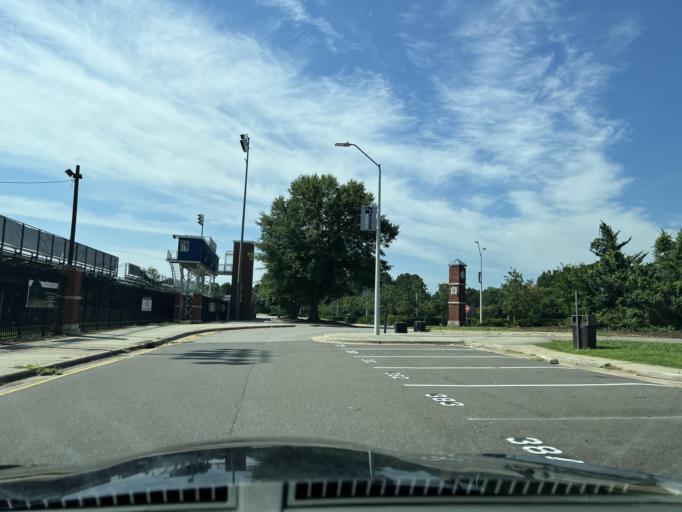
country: US
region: North Carolina
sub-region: Wake County
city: West Raleigh
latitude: 35.8655
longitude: -78.6024
